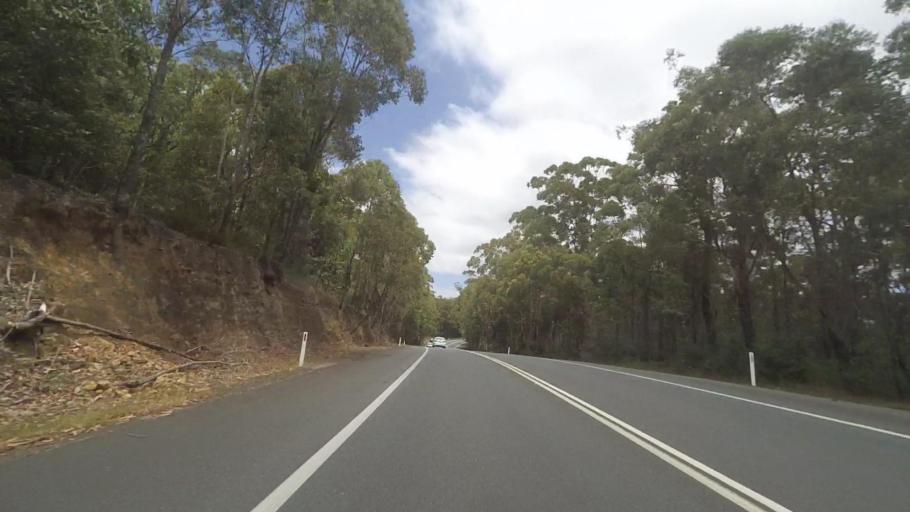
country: AU
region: New South Wales
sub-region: Shoalhaven Shire
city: Milton
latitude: -35.1547
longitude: 150.4508
